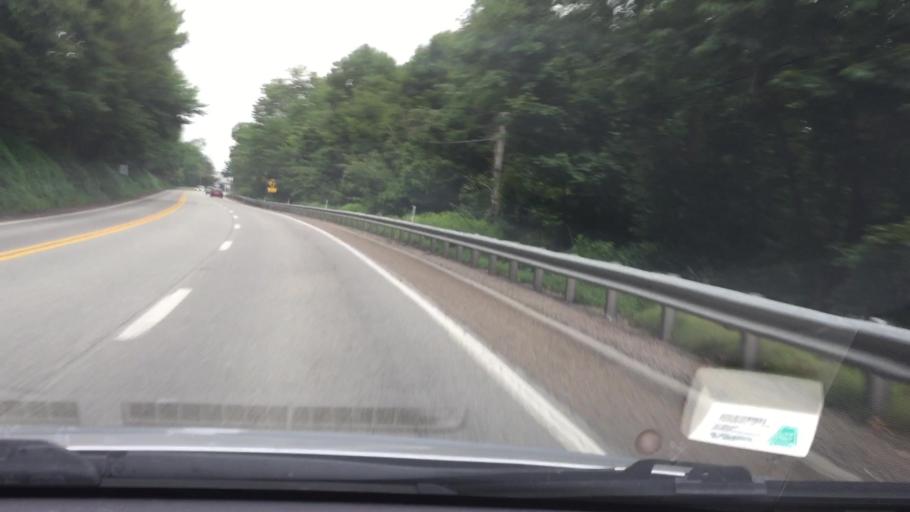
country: US
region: Pennsylvania
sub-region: Armstrong County
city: Freeport
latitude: 40.6830
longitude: -79.6951
